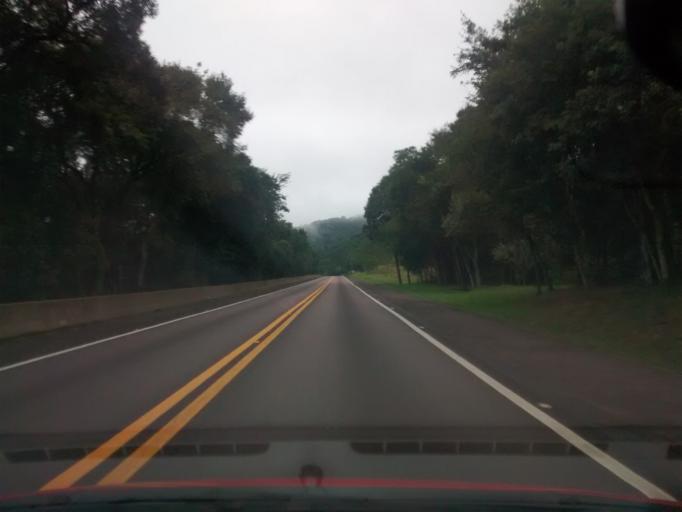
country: BR
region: Rio Grande do Sul
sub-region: Vacaria
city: Estrela
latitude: -28.1979
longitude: -50.7490
